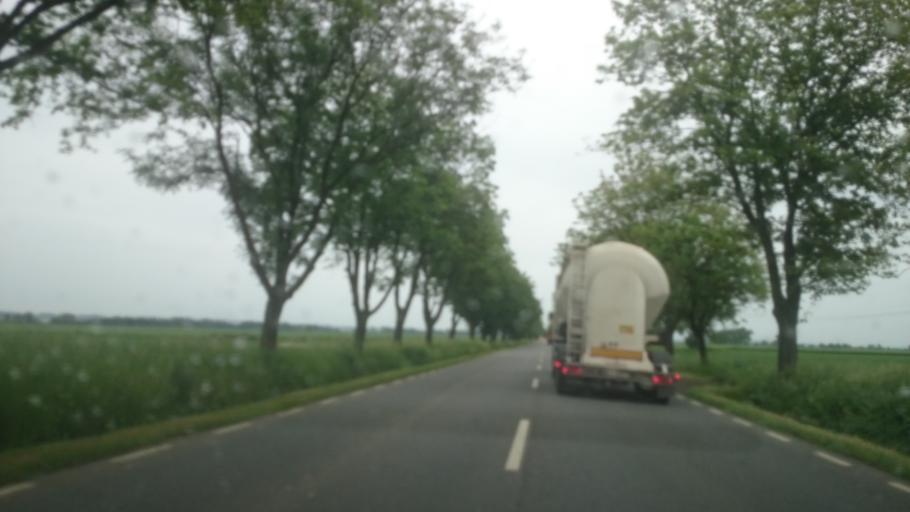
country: PL
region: Opole Voivodeship
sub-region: Powiat nyski
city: Paczkow
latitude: 50.4526
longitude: 17.0544
